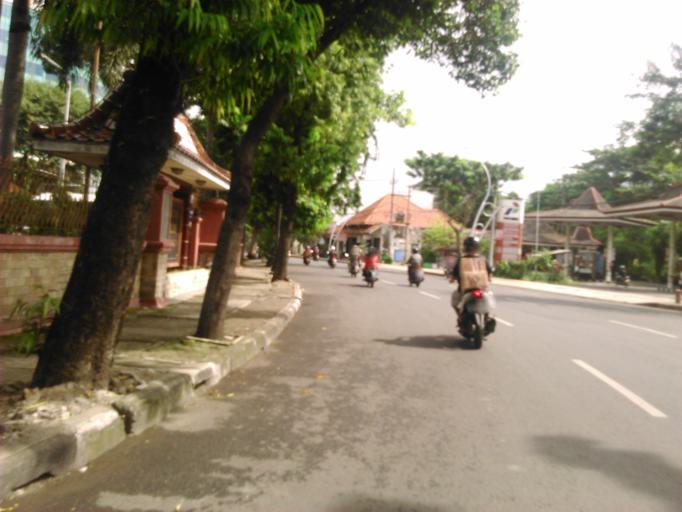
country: ID
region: East Java
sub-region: Kota Surabaya
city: Surabaya
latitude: -7.2575
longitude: 112.7437
